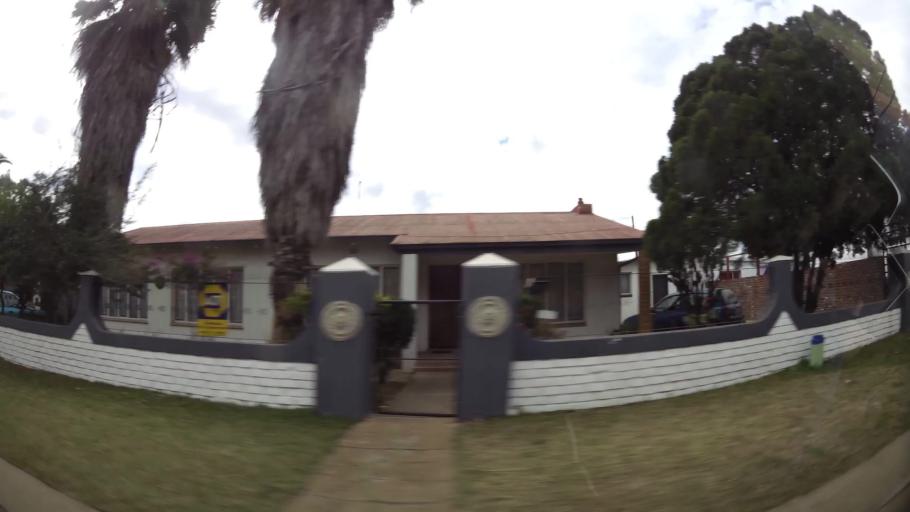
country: ZA
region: Gauteng
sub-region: City of Tshwane Metropolitan Municipality
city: Pretoria
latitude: -25.7165
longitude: 28.3130
